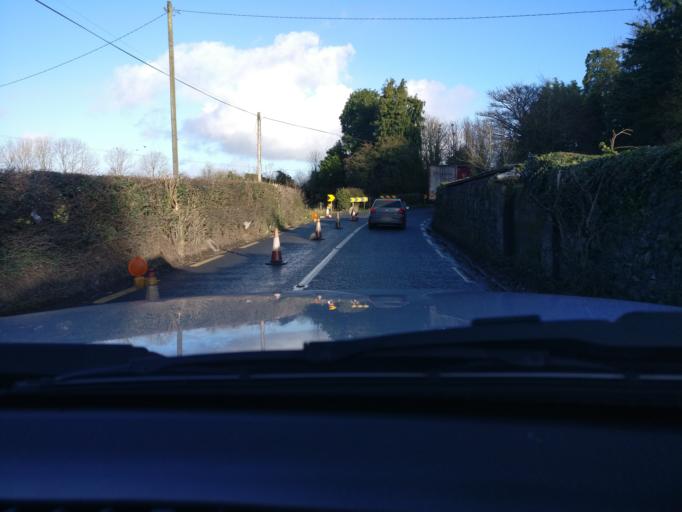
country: IE
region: Leinster
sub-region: An Iarmhi
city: Rathwire
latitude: 53.5807
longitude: -7.1511
